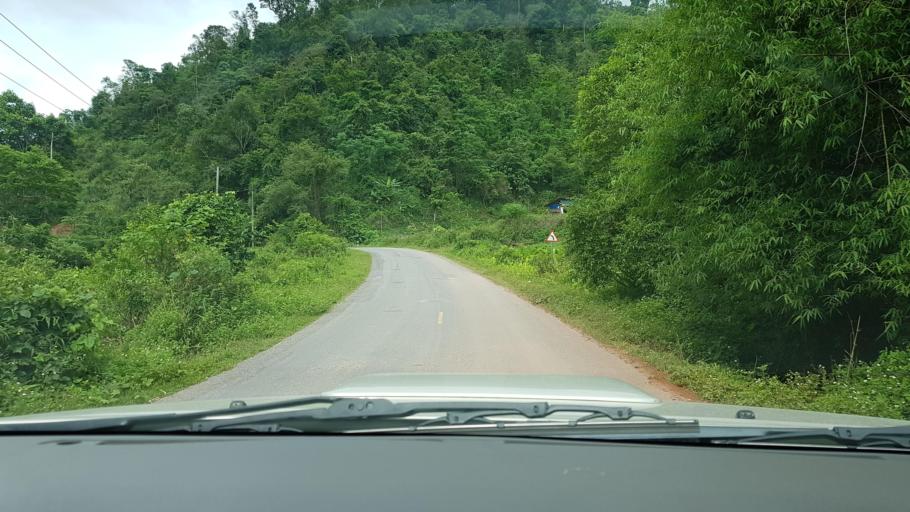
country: LA
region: Oudomxai
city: Muang Xay
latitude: 20.5576
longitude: 101.9124
